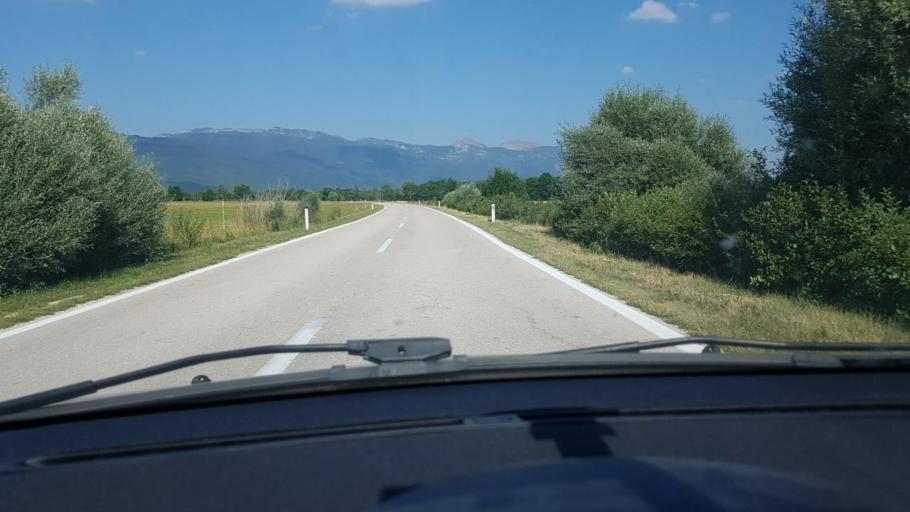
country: BA
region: Federation of Bosnia and Herzegovina
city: Glamoc
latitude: 43.9834
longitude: 16.6939
